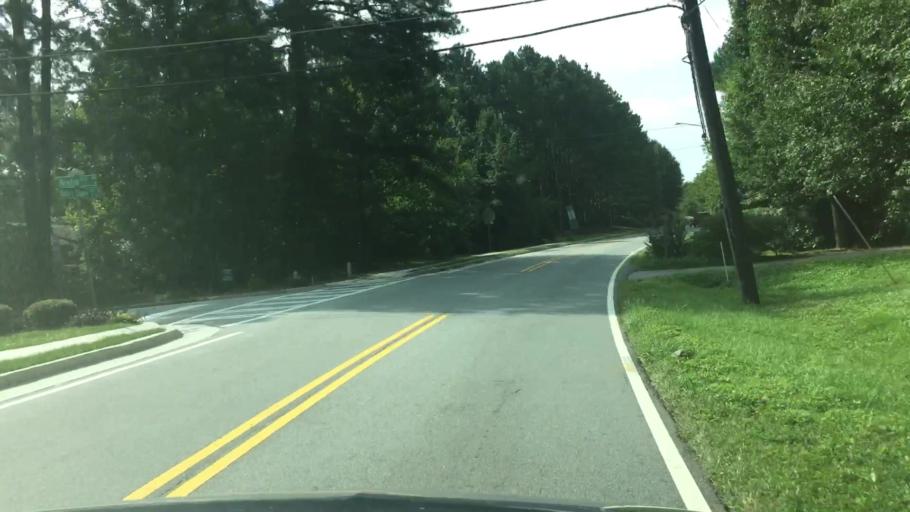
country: US
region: Georgia
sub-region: DeKalb County
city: Doraville
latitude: 33.9562
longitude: -84.2725
